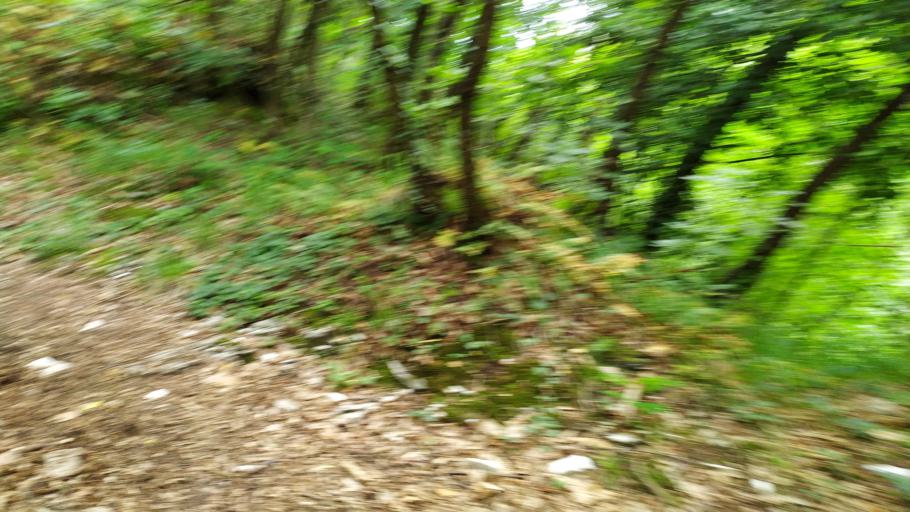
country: IT
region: Veneto
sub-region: Provincia di Vicenza
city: Torrebelvicino
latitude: 45.6902
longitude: 11.3237
